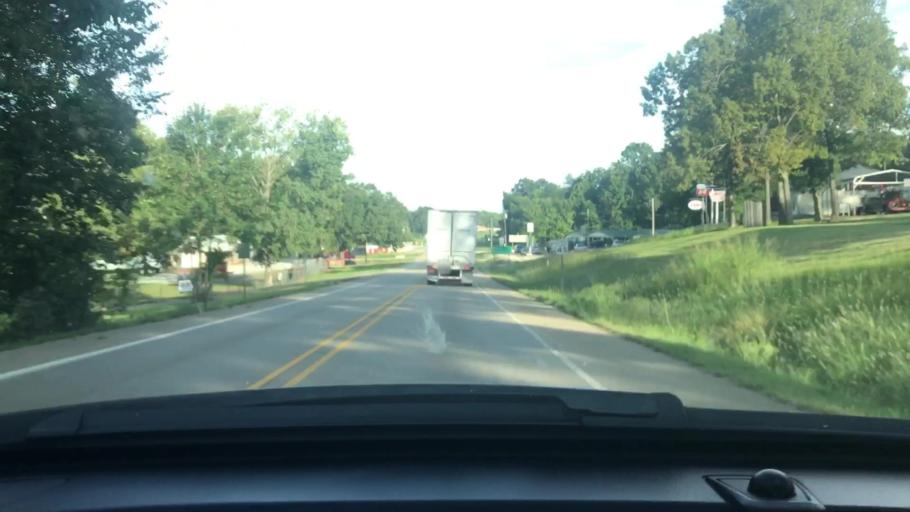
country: US
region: Arkansas
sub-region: Sharp County
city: Cherokee Village
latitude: 36.2378
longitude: -91.2563
